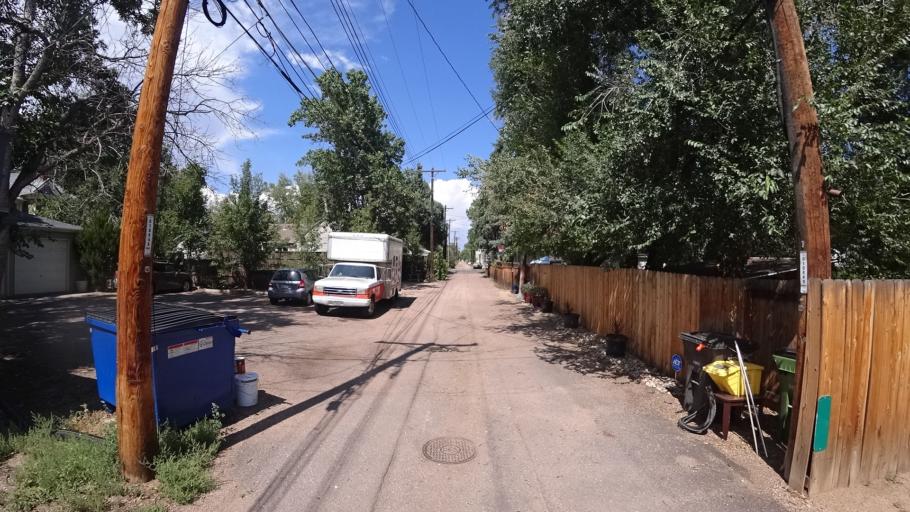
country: US
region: Colorado
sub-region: El Paso County
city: Colorado Springs
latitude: 38.8557
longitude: -104.8196
